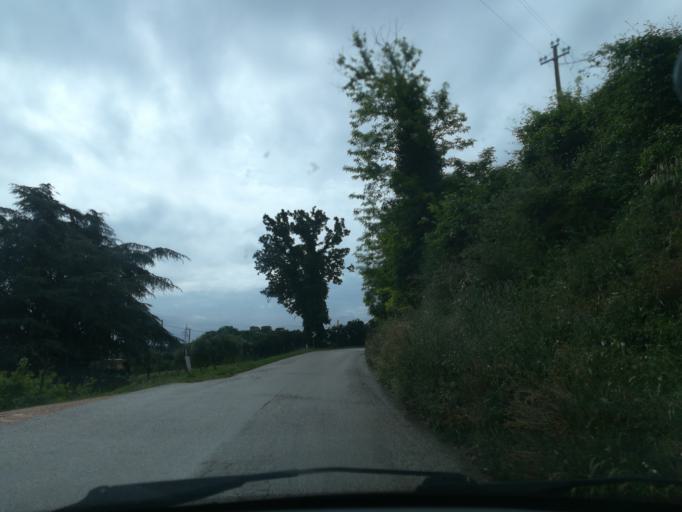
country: IT
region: The Marches
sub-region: Provincia di Macerata
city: Petriolo
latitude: 43.2279
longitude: 13.4632
